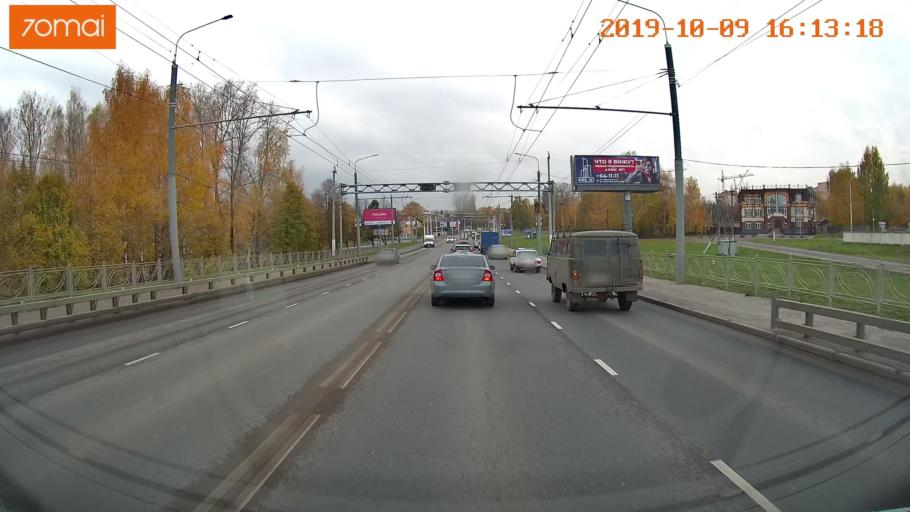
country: RU
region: Kostroma
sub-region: Kostromskoy Rayon
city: Kostroma
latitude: 57.7477
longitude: 40.9314
